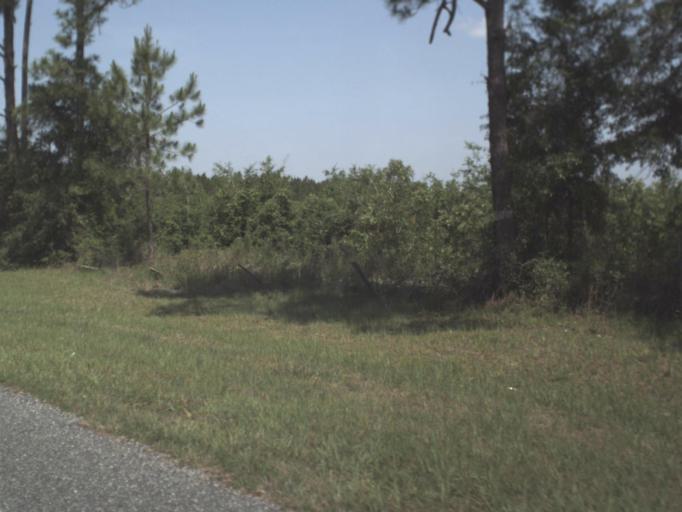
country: US
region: Florida
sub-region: Clay County
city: Middleburg
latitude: 29.9820
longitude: -81.9391
